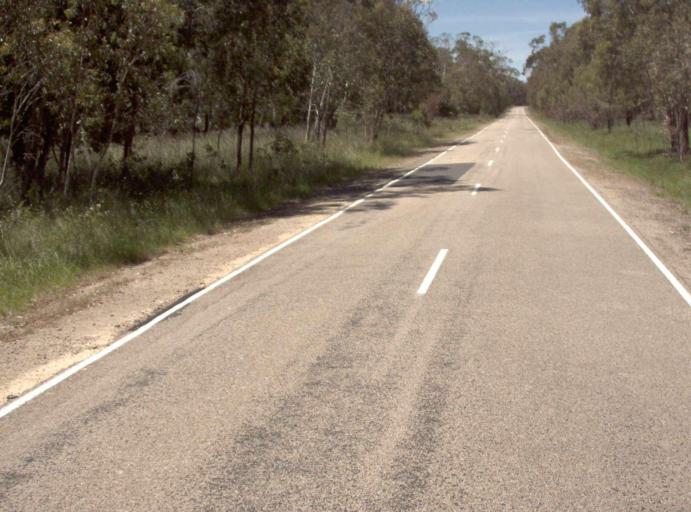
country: AU
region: Victoria
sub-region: East Gippsland
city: Lakes Entrance
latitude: -37.1533
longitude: 148.2562
